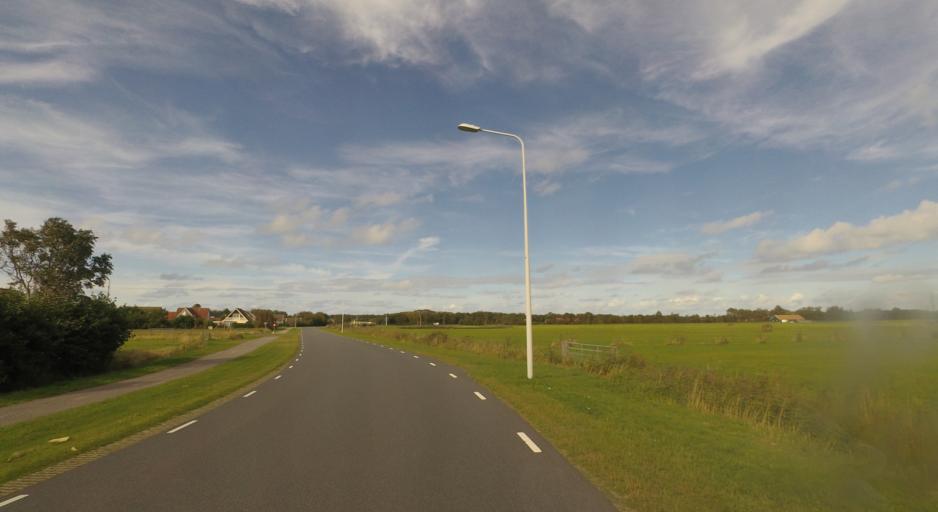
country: NL
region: Friesland
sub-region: Gemeente Ameland
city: Nes
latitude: 53.4439
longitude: 5.7824
